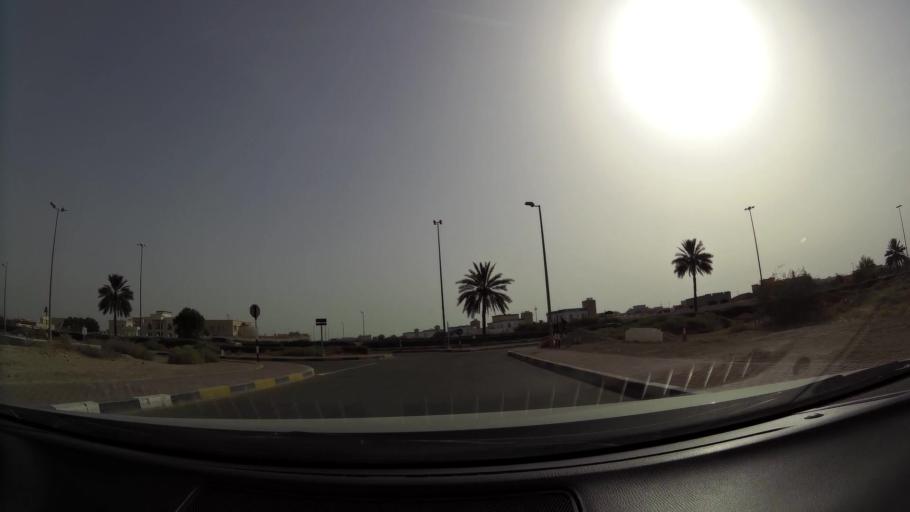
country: AE
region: Abu Dhabi
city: Al Ain
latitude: 24.1332
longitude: 55.7018
